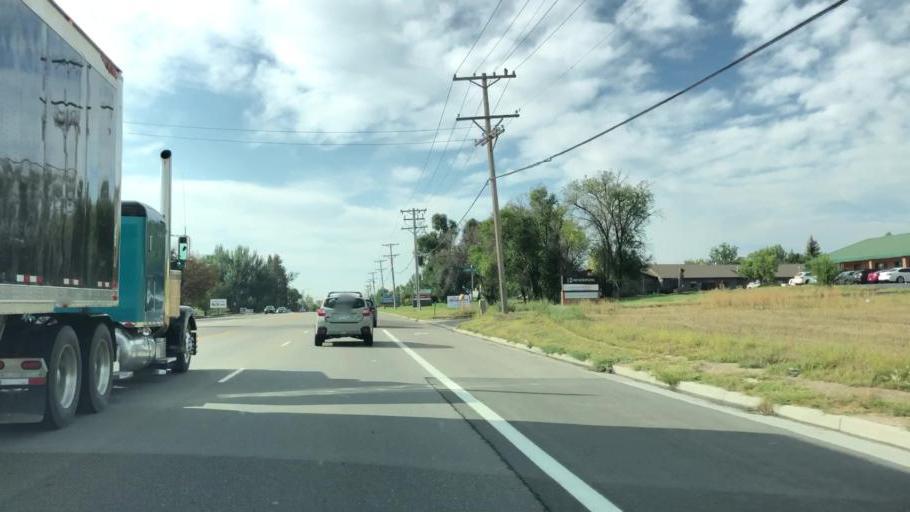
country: US
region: Colorado
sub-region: Larimer County
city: Loveland
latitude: 40.4477
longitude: -105.0775
